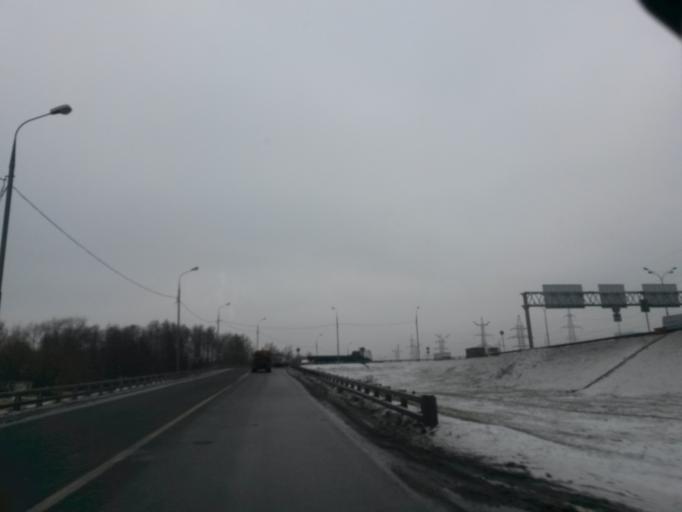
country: RU
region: Moscow
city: Mikhalkovo
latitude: 55.6685
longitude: 37.4265
